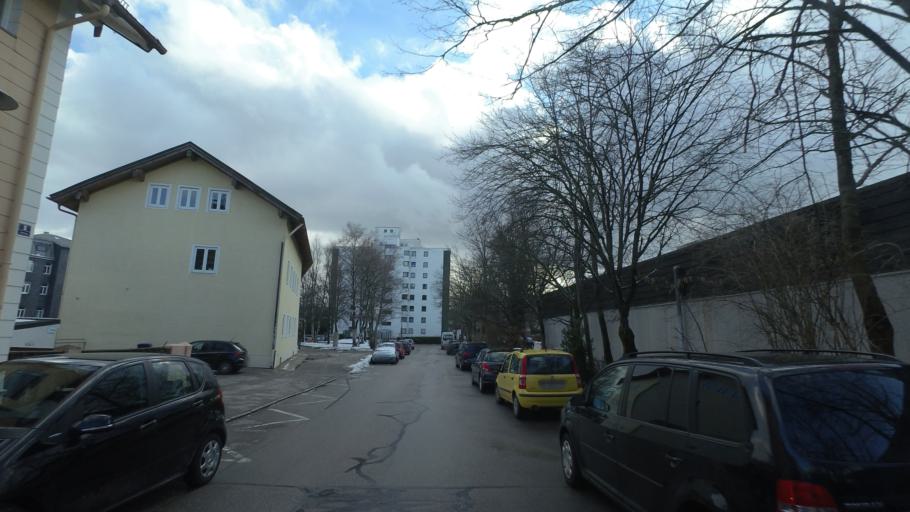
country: DE
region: Bavaria
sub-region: Upper Bavaria
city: Traunstein
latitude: 47.8719
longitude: 12.6385
